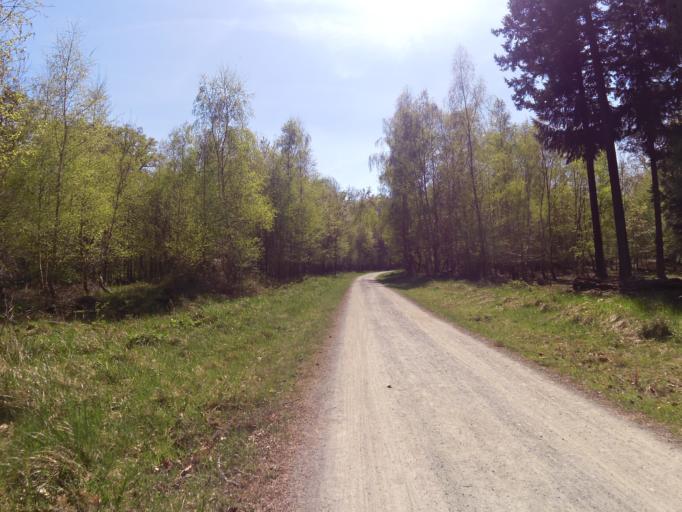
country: DE
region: Hesse
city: Morfelden-Walldorf
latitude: 49.9831
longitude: 8.5202
